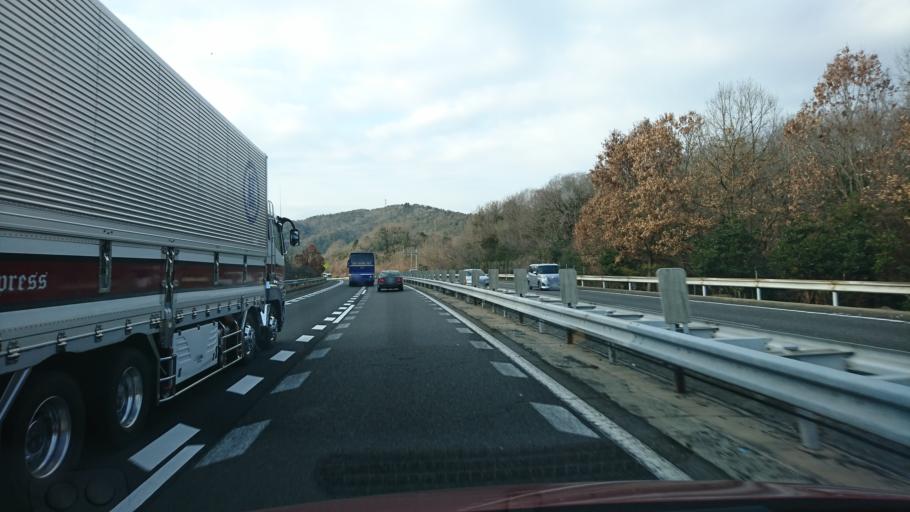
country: JP
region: Hyogo
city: Aioi
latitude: 34.8047
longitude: 134.4401
